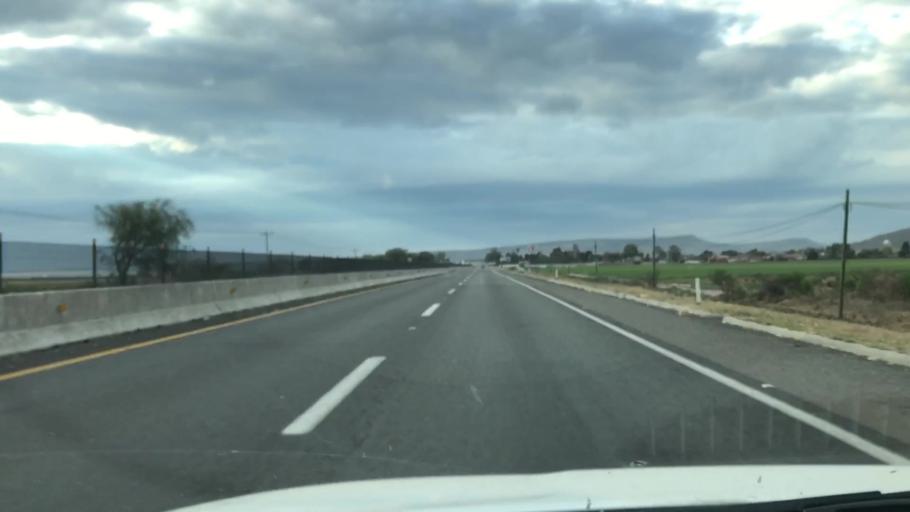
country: MX
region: Guanajuato
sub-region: Penjamo
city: Estacion la Piedad
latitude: 20.3863
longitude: -101.9125
